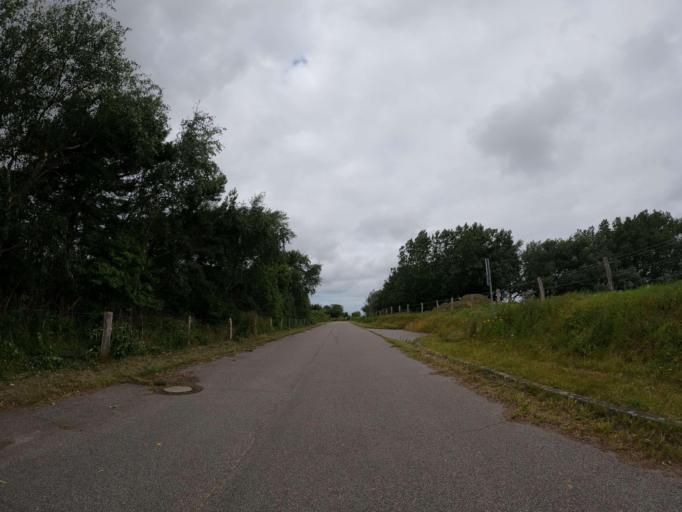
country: DE
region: Schleswig-Holstein
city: Tinnum
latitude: 54.9207
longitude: 8.3461
